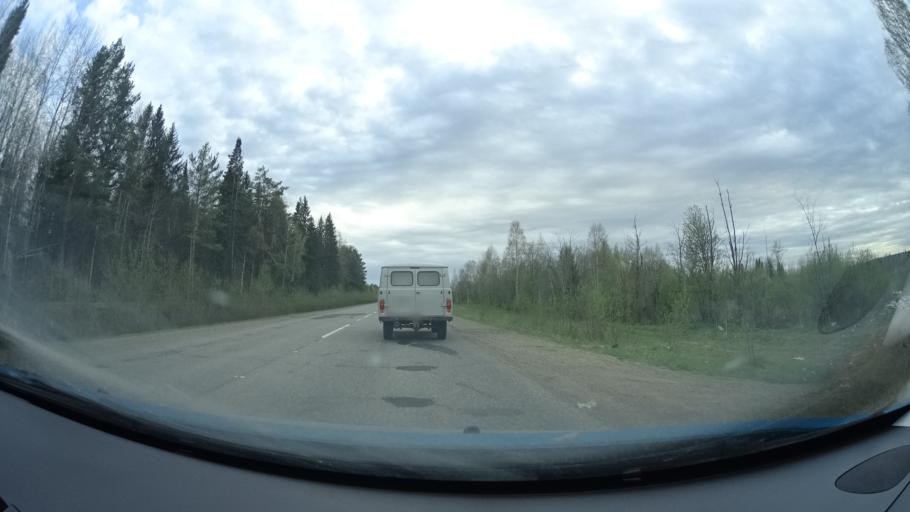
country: RU
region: Perm
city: Osa
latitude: 57.4459
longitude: 55.6450
